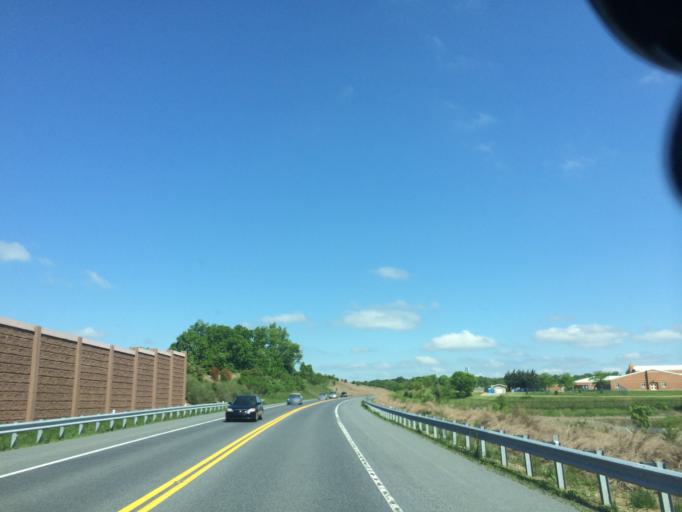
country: US
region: Maryland
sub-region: Carroll County
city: Hampstead
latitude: 39.5964
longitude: -76.8604
